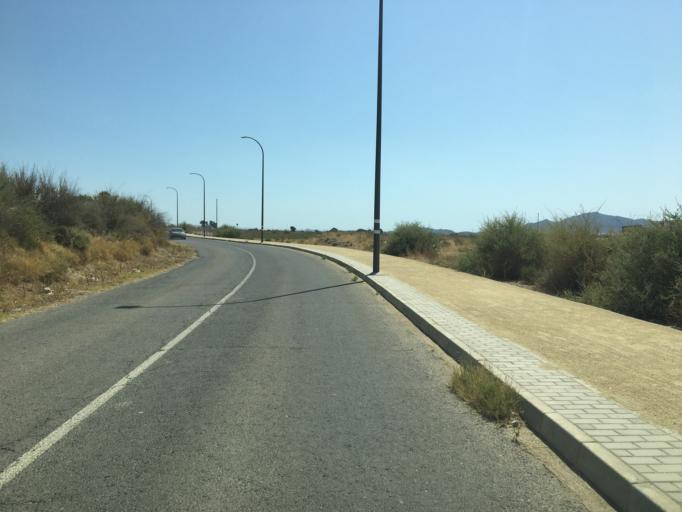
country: ES
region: Andalusia
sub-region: Provincia de Almeria
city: Huercal-Overa
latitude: 37.4039
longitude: -1.9357
